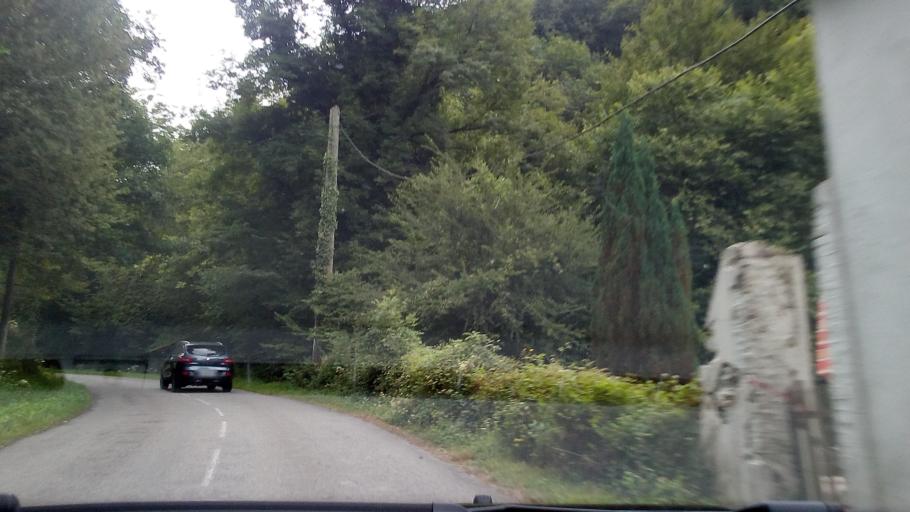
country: FR
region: Aquitaine
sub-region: Departement des Pyrenees-Atlantiques
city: Ogeu-les-Bains
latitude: 43.0801
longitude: -0.5677
